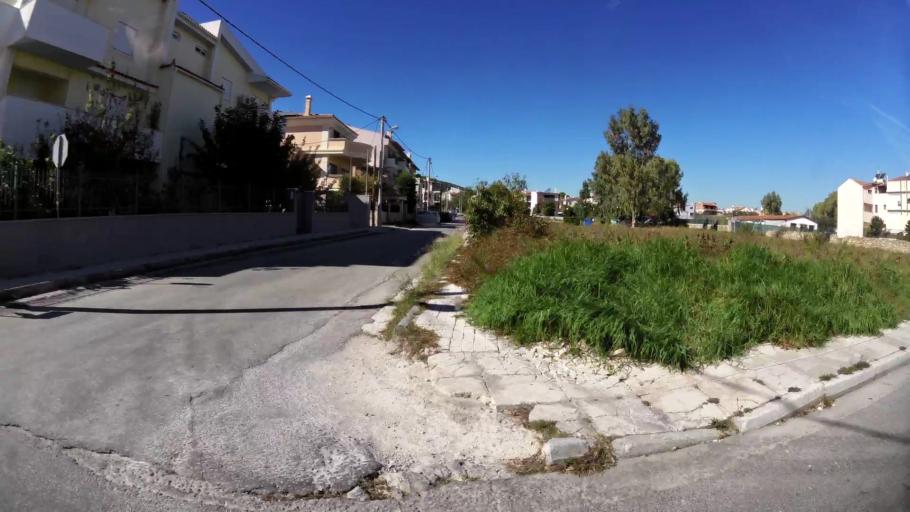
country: GR
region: Attica
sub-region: Nomarchia Anatolikis Attikis
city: Gerakas
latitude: 38.0051
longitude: 23.8579
